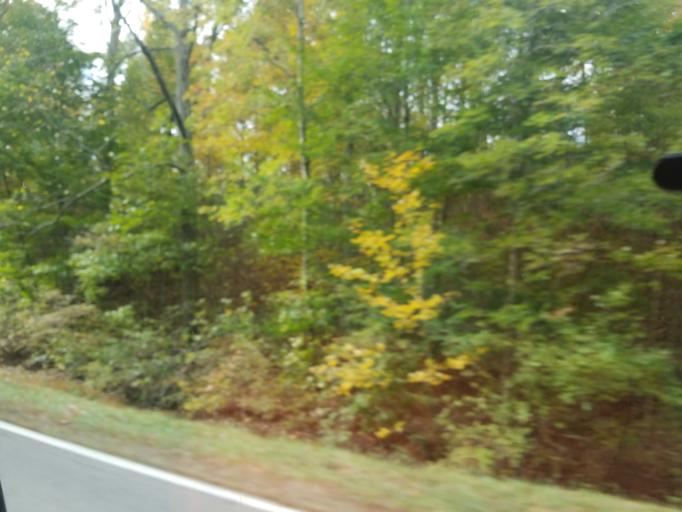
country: US
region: Ohio
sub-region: Vinton County
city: McArthur
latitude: 39.1682
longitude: -82.4386
